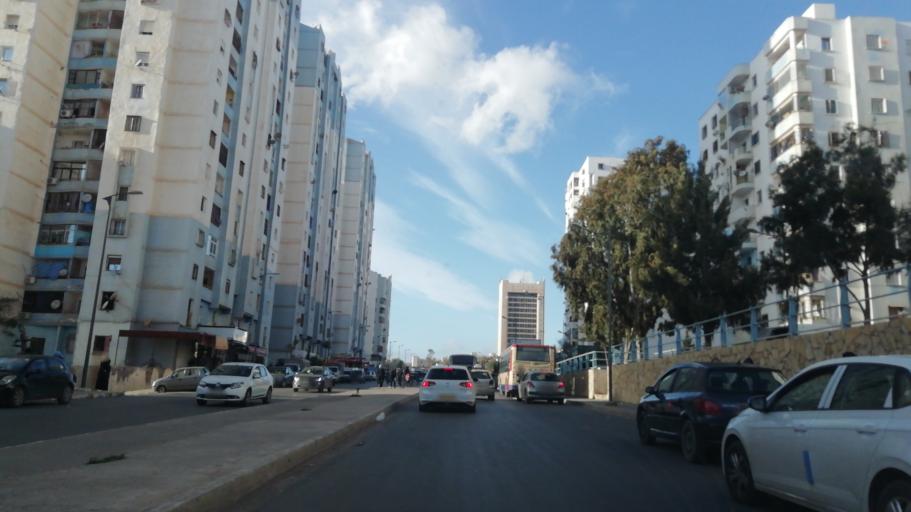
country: DZ
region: Oran
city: Bir el Djir
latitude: 35.7008
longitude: -0.5751
